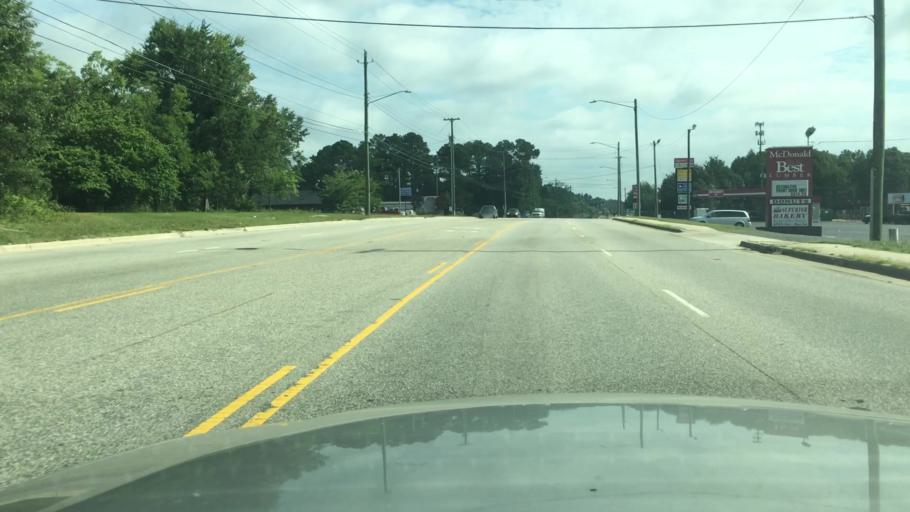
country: US
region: North Carolina
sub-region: Cumberland County
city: Hope Mills
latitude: 35.0096
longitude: -78.9666
